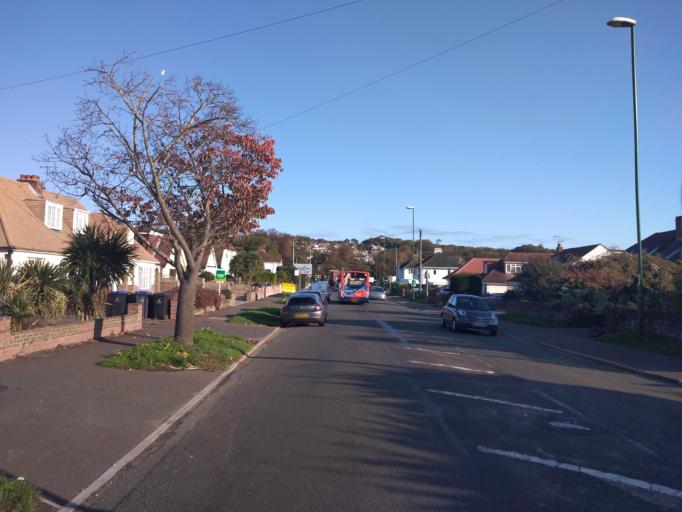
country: GB
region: England
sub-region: West Sussex
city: Lancing
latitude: 50.8352
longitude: -0.3177
